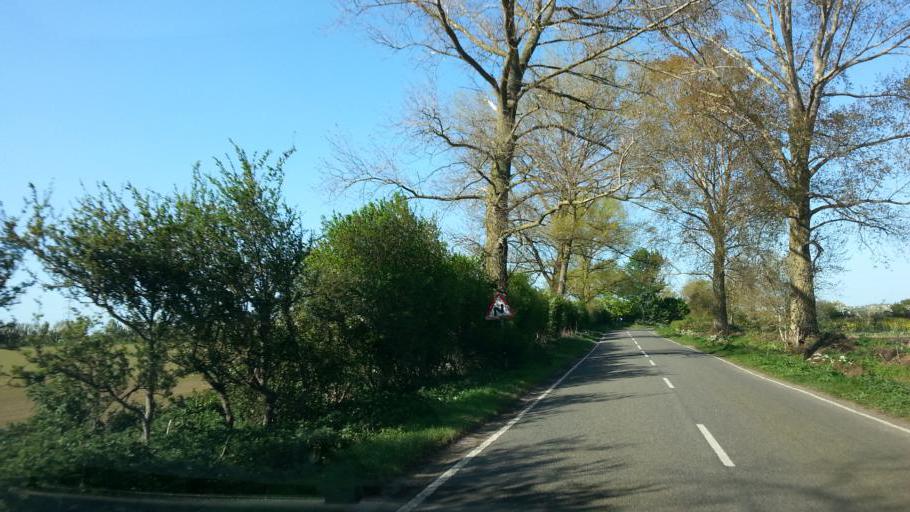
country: GB
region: England
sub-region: Lincolnshire
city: Great Gonerby
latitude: 52.9709
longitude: -0.6866
